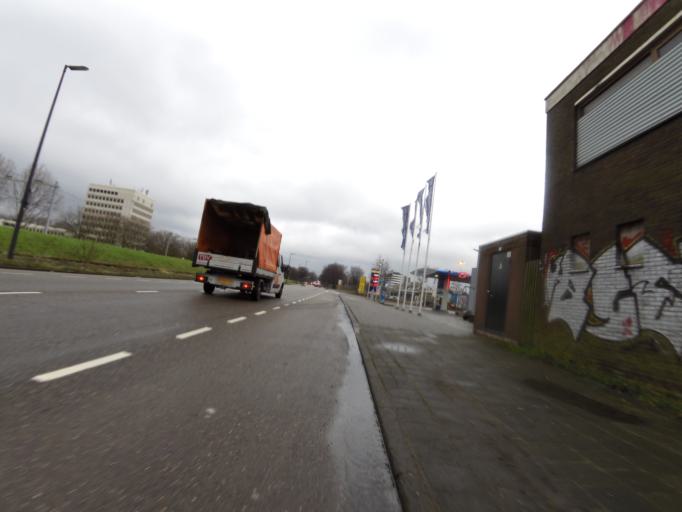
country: NL
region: South Holland
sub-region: Gemeente Vlaardingen
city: Vlaardingen
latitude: 51.9009
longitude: 4.3328
